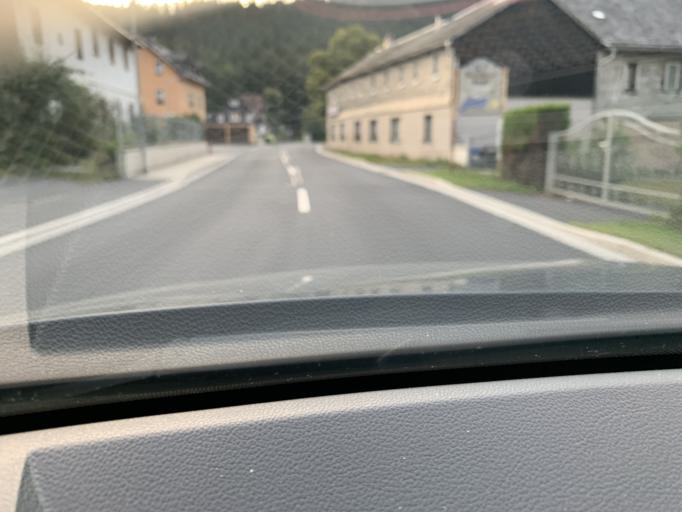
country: DE
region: Thuringia
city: Judenbach
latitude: 50.3992
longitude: 11.2001
